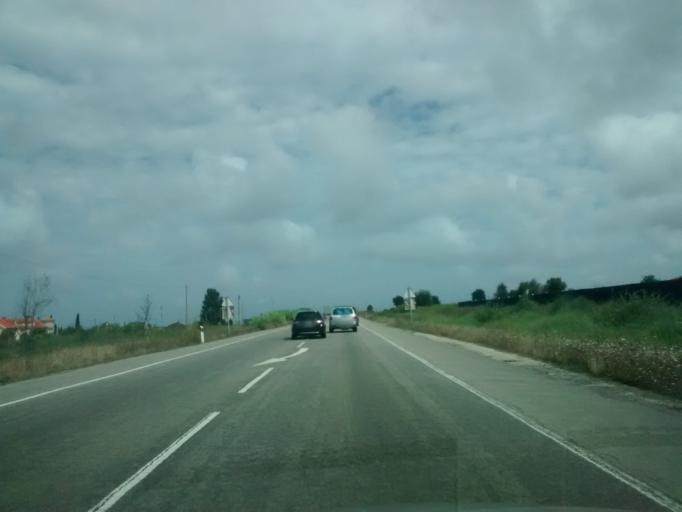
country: PT
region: Aveiro
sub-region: Aveiro
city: Oliveirinha
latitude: 40.5863
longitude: -8.6069
